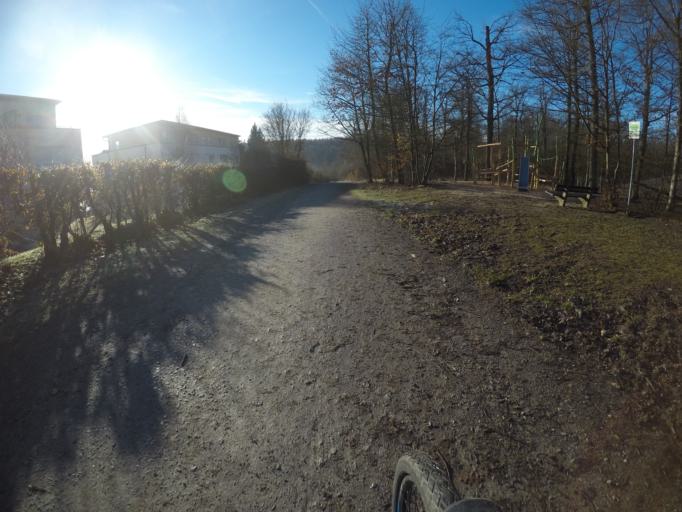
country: DE
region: Baden-Wuerttemberg
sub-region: Regierungsbezirk Stuttgart
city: Boeblingen
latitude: 48.6667
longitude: 8.9999
